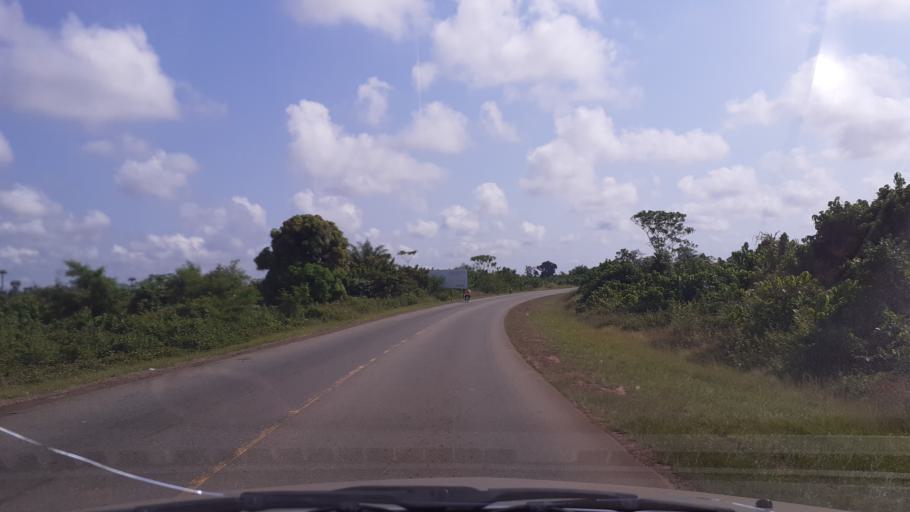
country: LR
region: Montserrado
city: Bensonville City
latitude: 6.2288
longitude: -10.5297
